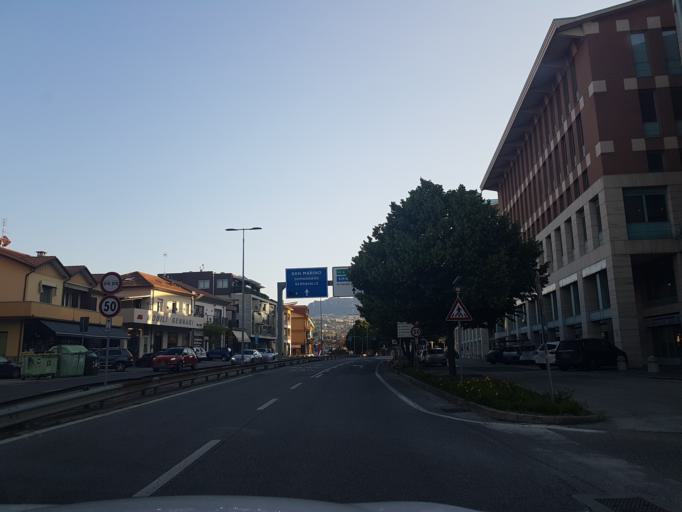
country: SM
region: Serravalle
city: Serravalle
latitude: 43.9811
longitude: 12.4896
